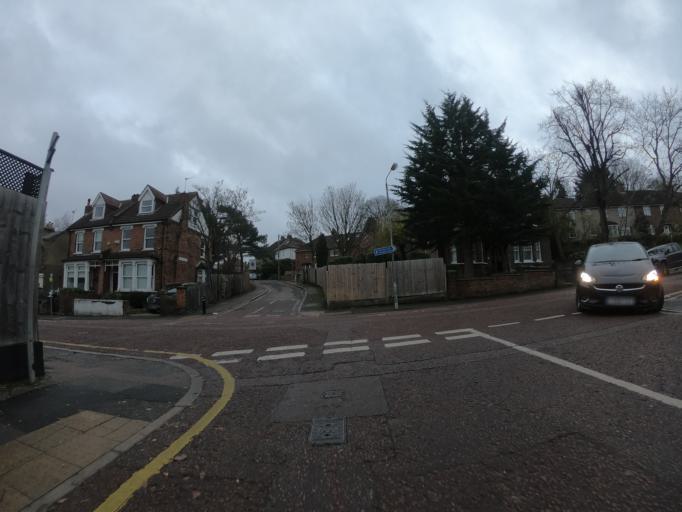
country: GB
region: England
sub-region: Greater London
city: Woolwich
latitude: 51.4872
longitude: 0.0388
